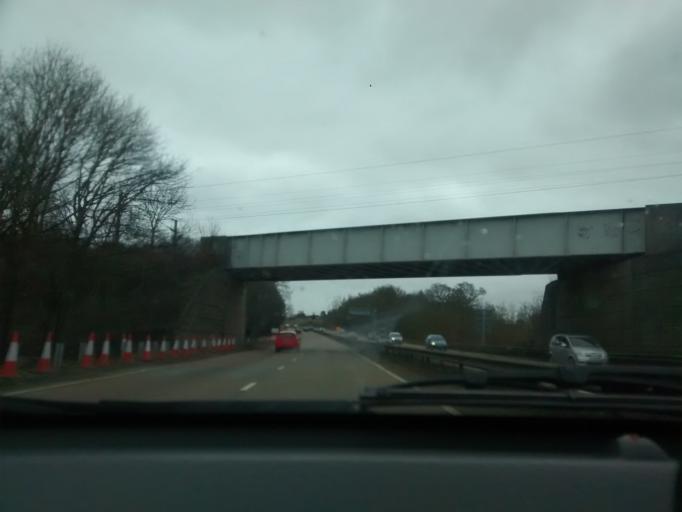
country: GB
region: England
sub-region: Suffolk
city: Ipswich
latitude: 52.0261
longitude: 1.1290
